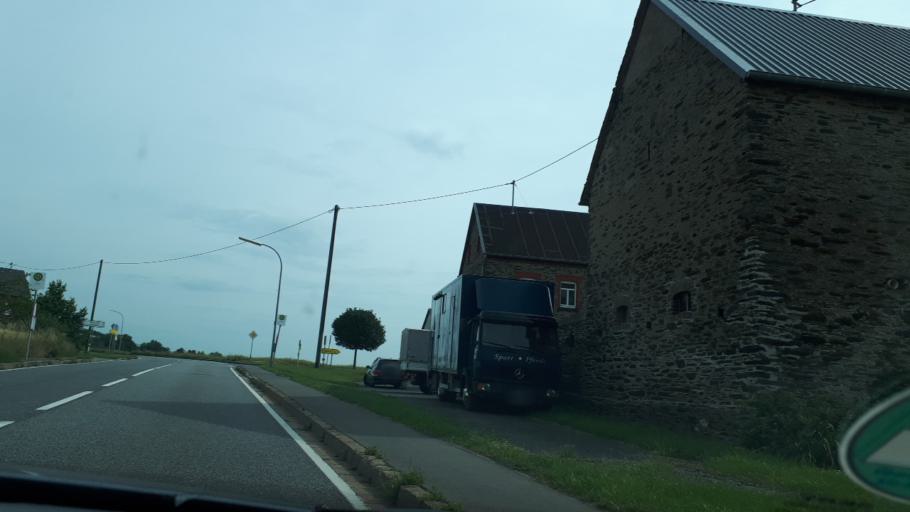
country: DE
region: Rheinland-Pfalz
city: Welling
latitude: 50.3318
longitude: 7.3043
